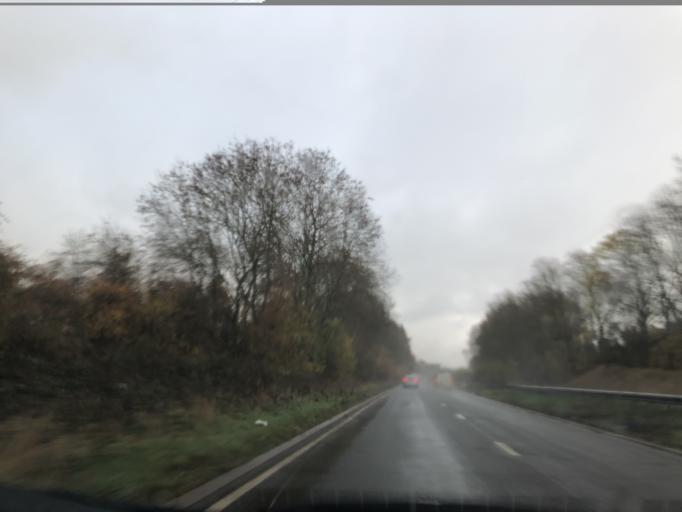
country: GB
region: England
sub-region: Solihull
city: Meriden
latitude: 52.4399
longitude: -1.6212
